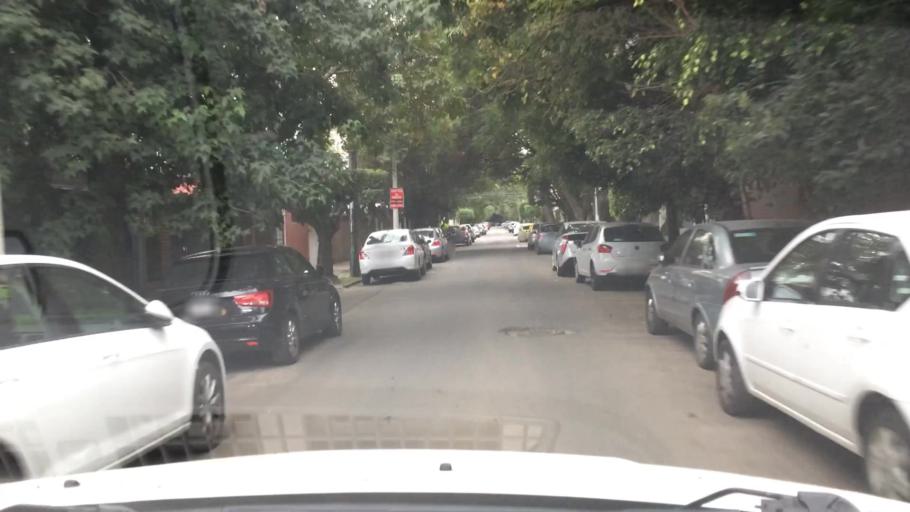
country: MX
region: Mexico City
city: Alvaro Obregon
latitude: 19.3565
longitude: -99.1890
